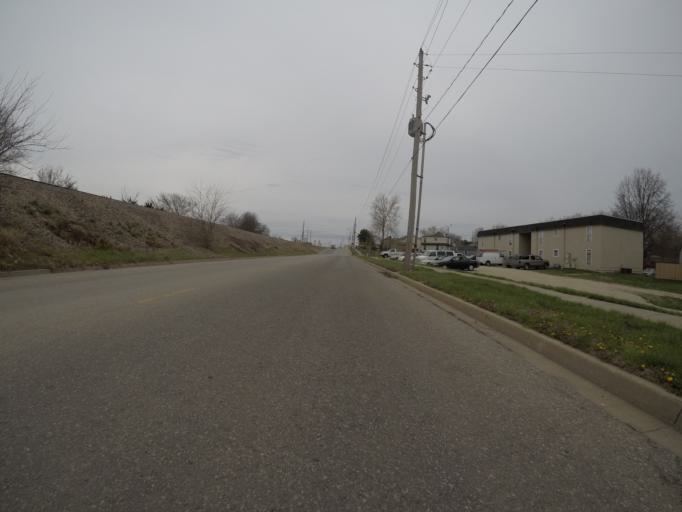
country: US
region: Kansas
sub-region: Johnson County
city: Olathe
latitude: 38.8719
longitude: -94.8070
